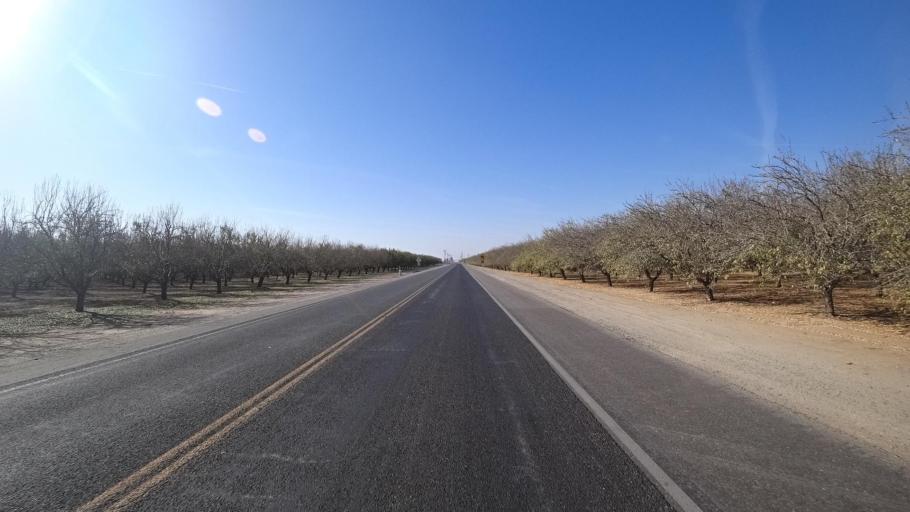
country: US
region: California
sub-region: Kern County
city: McFarland
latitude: 35.6456
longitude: -119.1972
